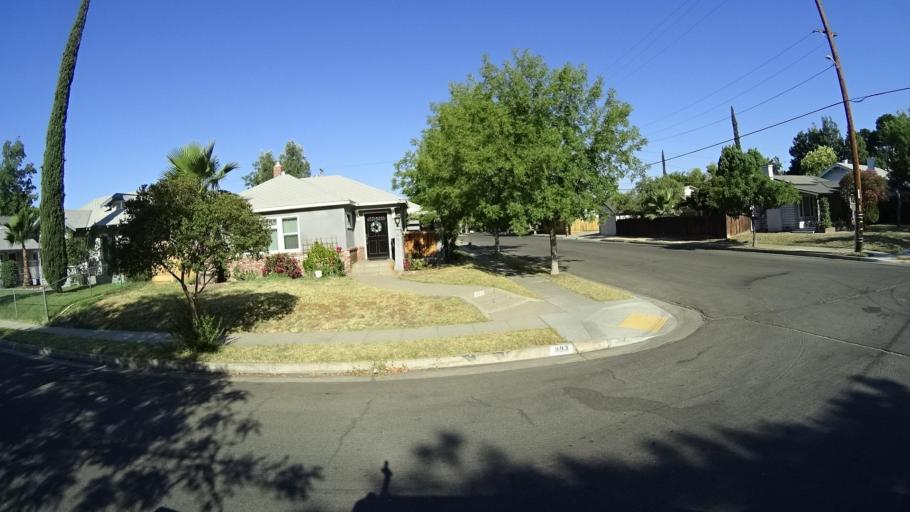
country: US
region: California
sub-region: Fresno County
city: Fresno
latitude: 36.7556
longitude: -119.8120
